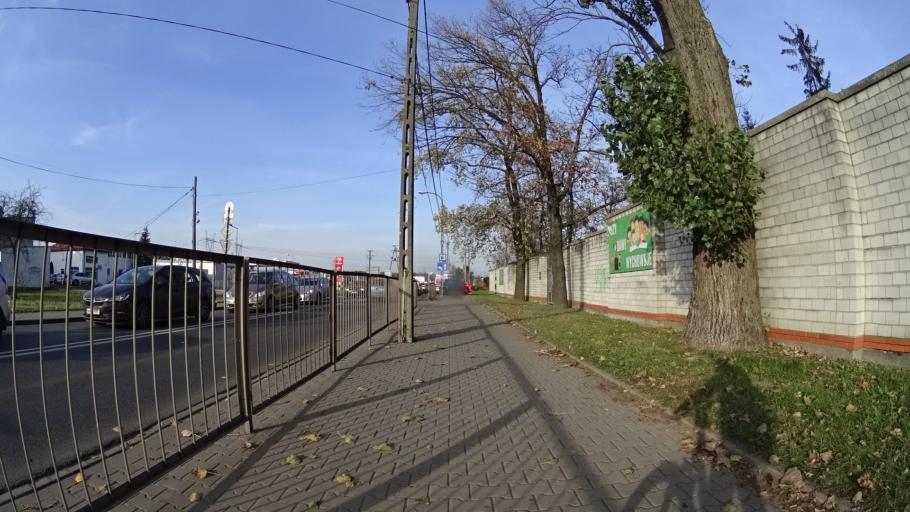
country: PL
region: Masovian Voivodeship
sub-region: Powiat warszawski zachodni
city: Babice
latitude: 52.2875
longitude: 20.8766
